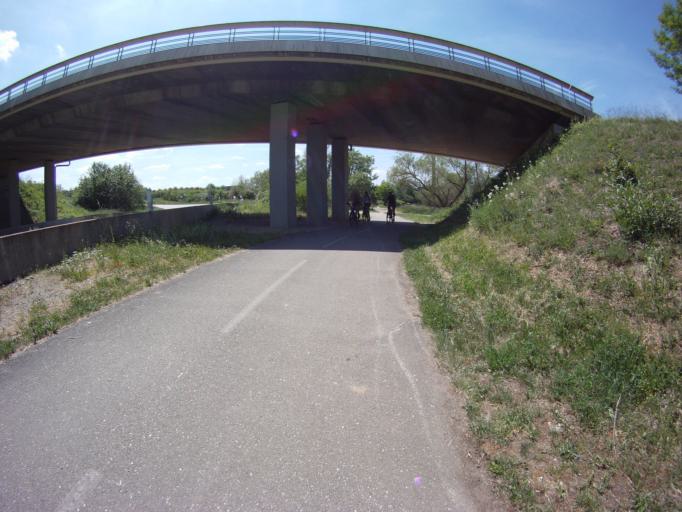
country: FR
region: Lorraine
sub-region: Departement de Meurthe-et-Moselle
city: Lay-Saint-Christophe
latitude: 48.7439
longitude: 6.1848
